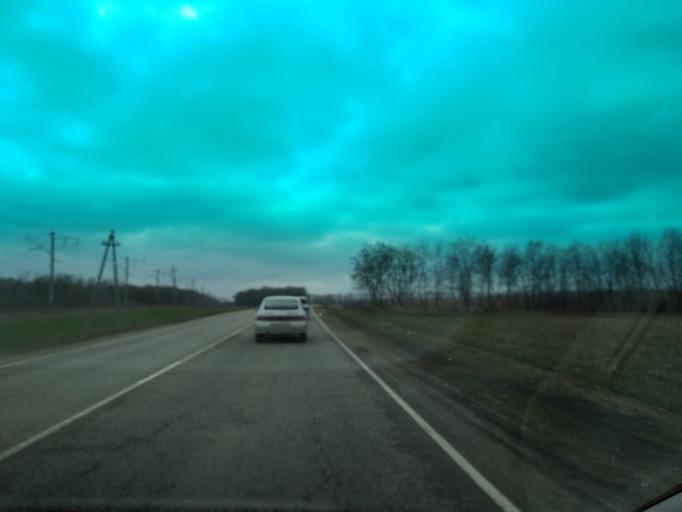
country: RU
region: Krasnodarskiy
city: Novorozhdestvenskaya
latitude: 45.8020
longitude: 39.9854
